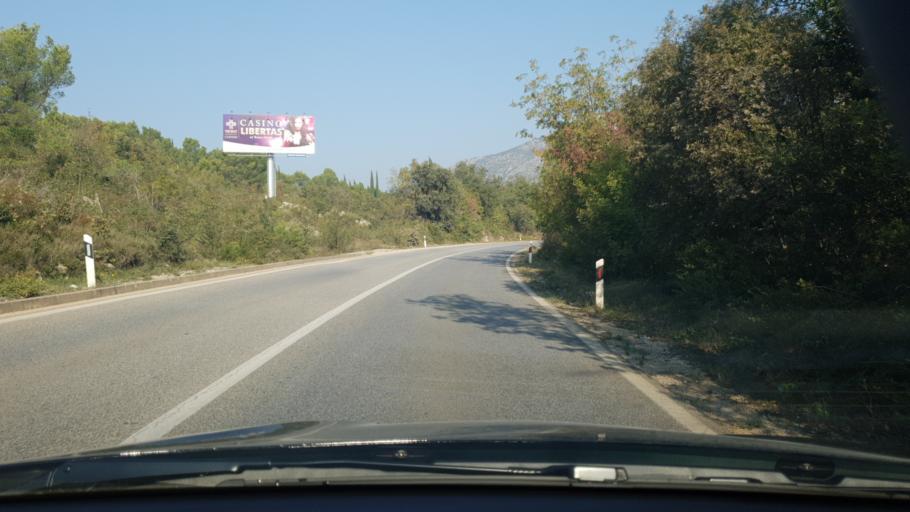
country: HR
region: Dubrovacko-Neretvanska
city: Cavtat
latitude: 42.5663
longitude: 18.2450
